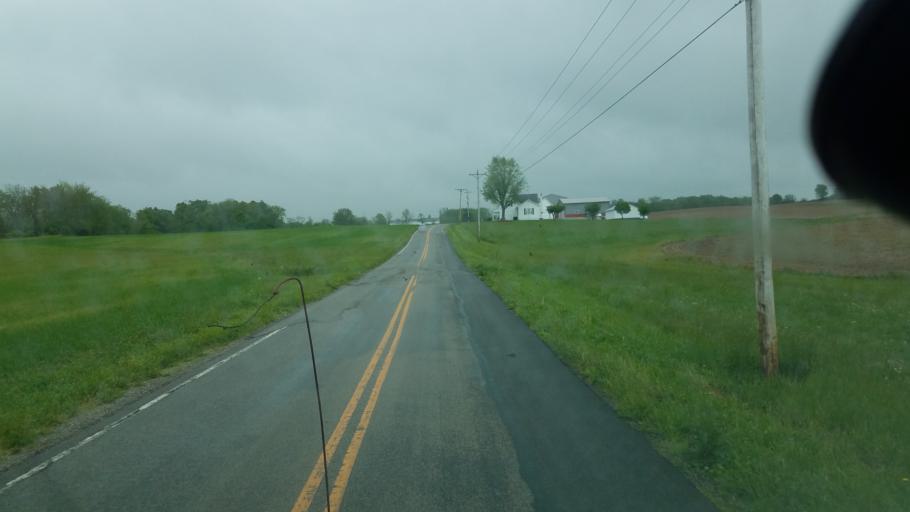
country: US
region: Ohio
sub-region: Highland County
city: Greenfield
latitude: 39.3407
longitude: -83.4481
